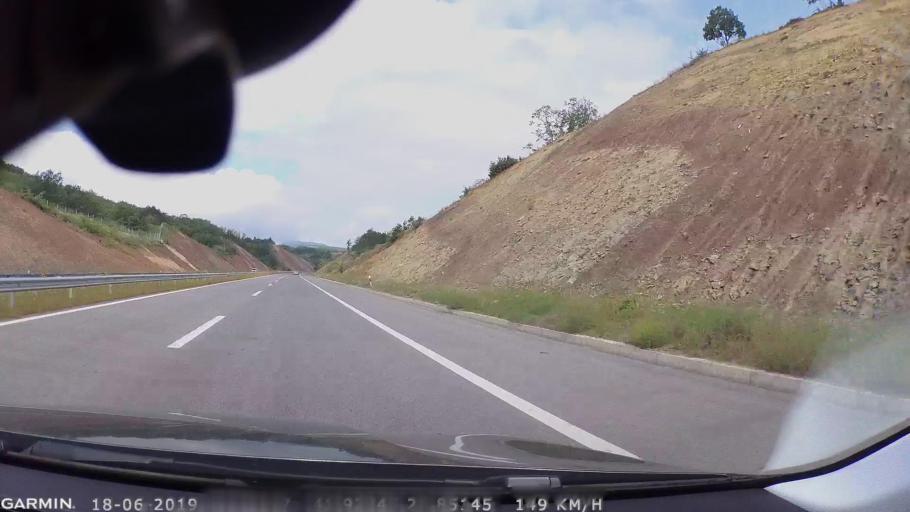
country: MK
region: Sveti Nikole
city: Gorobinci
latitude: 41.9171
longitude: 21.8804
